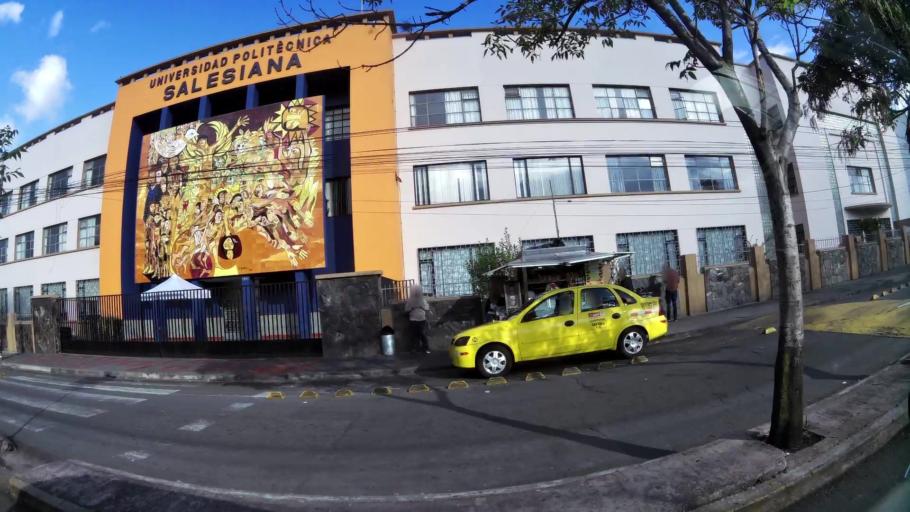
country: EC
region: Pichincha
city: Quito
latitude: -0.2084
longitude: -78.4885
